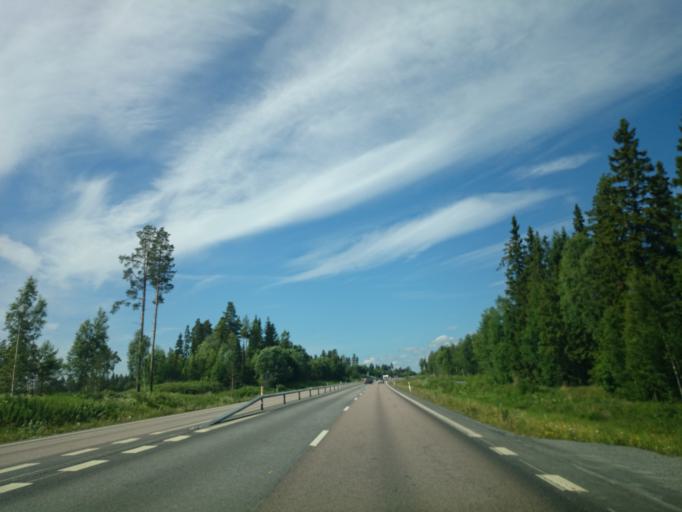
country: SE
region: Jaemtland
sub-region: Krokoms Kommun
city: Krokom
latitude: 63.2897
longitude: 14.5081
